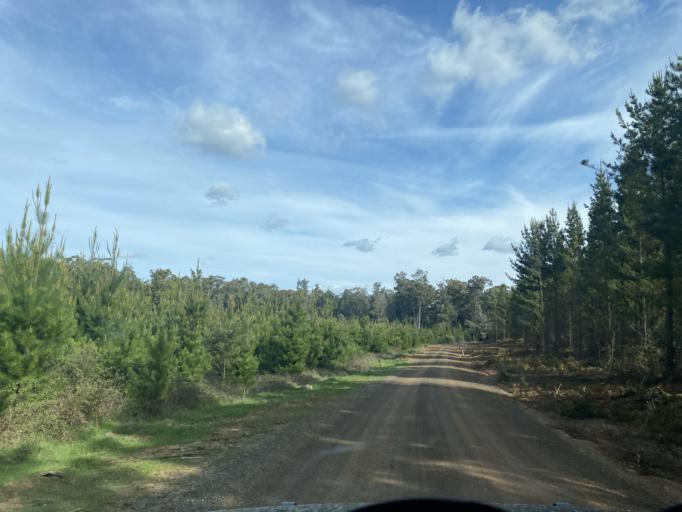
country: AU
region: Victoria
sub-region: Mansfield
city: Mansfield
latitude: -36.8397
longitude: 146.1826
